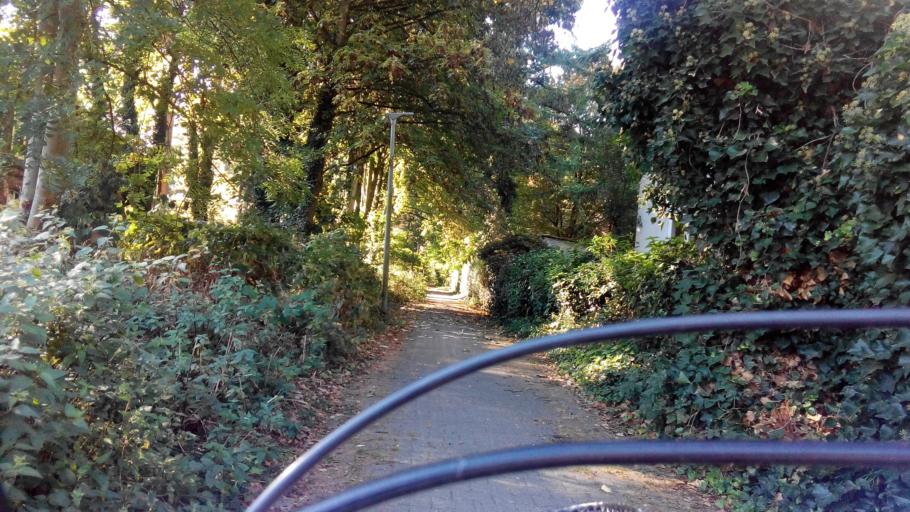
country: DE
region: North Rhine-Westphalia
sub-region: Regierungsbezirk Munster
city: Gelsenkirchen
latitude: 51.4945
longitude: 7.1176
